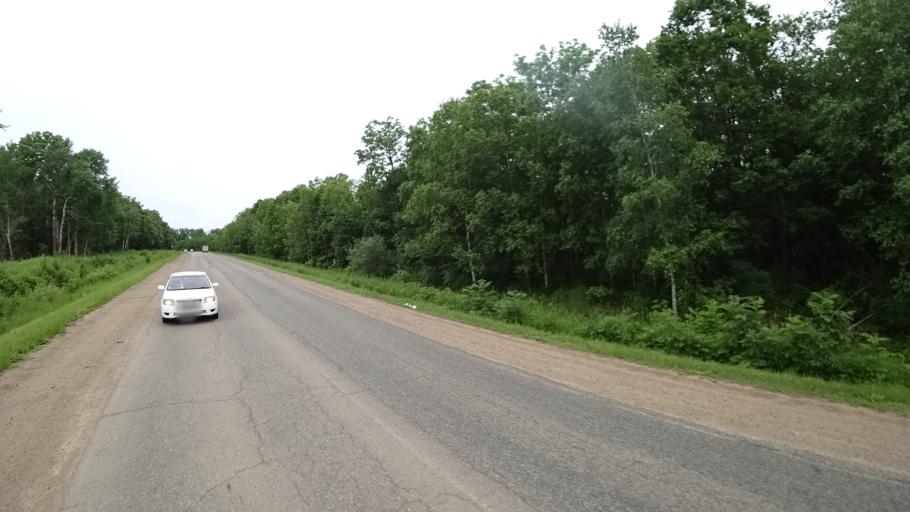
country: RU
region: Primorskiy
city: Novosysoyevka
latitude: 44.1863
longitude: 133.3533
